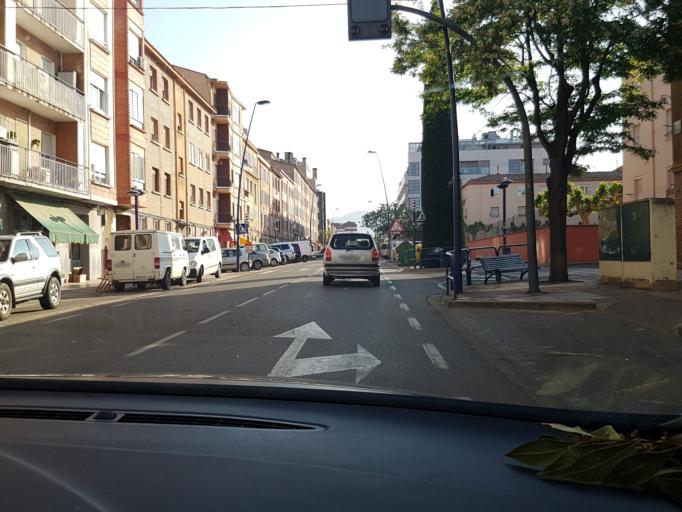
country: ES
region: La Rioja
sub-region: Provincia de La Rioja
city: Arnedo
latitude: 42.2259
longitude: -2.0980
